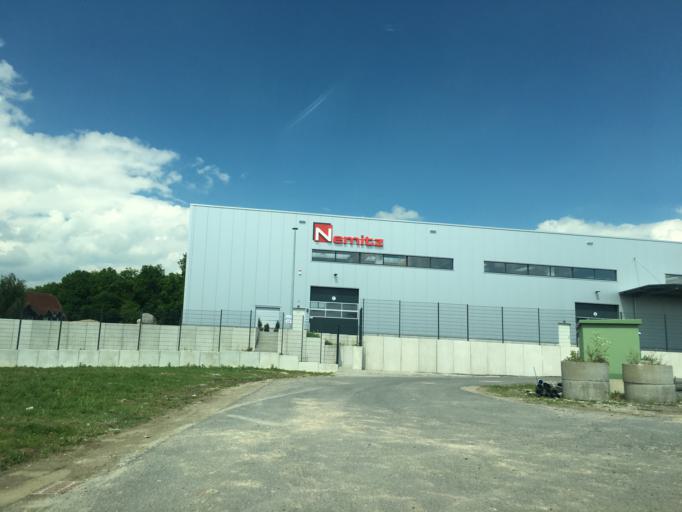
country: DE
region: North Rhine-Westphalia
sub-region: Regierungsbezirk Munster
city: Altenberge
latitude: 52.0357
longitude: 7.4628
